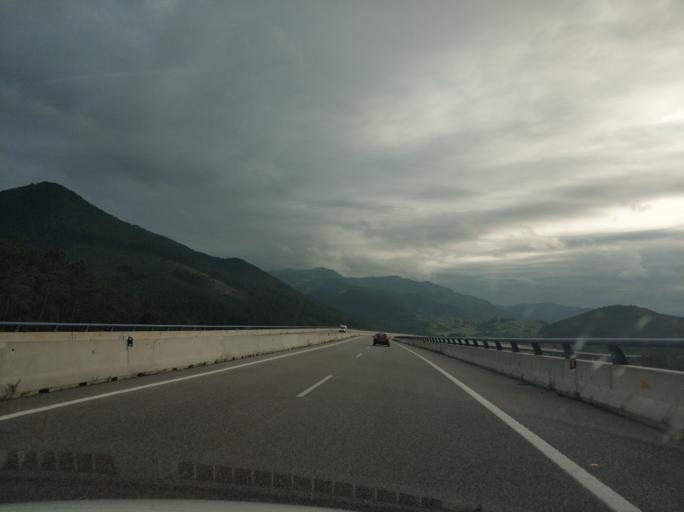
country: ES
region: Asturias
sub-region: Province of Asturias
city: Cudillero
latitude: 43.5572
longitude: -6.1860
